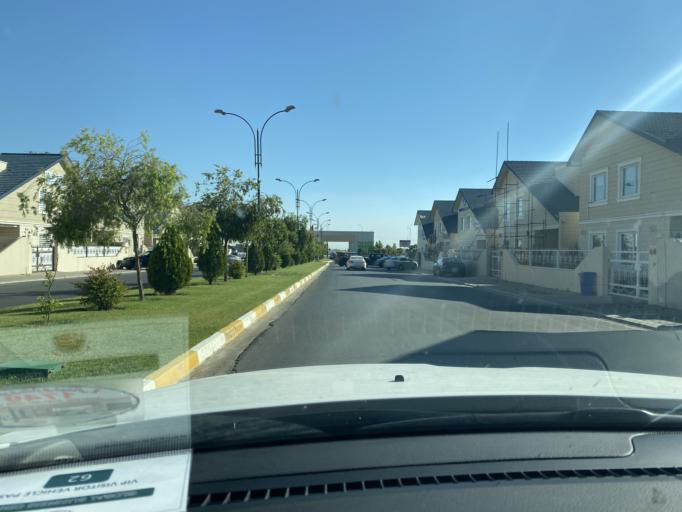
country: IQ
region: Arbil
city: Erbil
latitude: 36.2403
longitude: 44.0501
